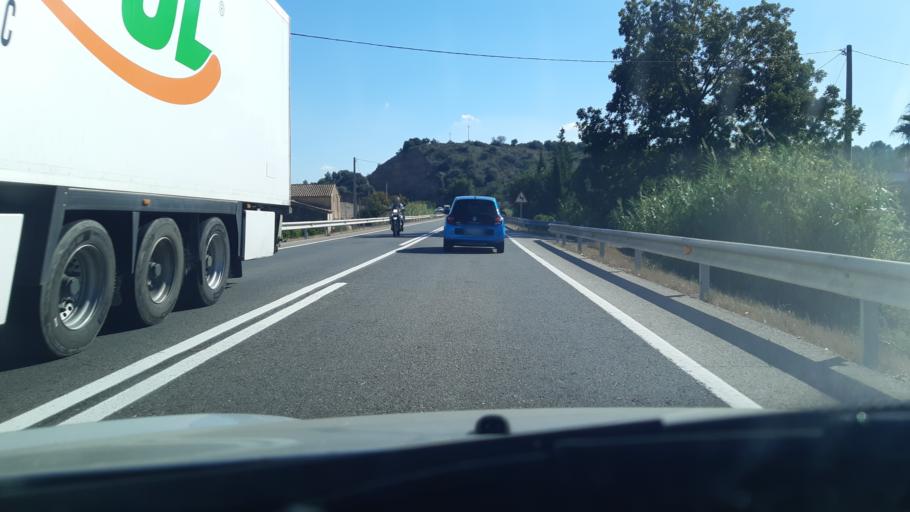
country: ES
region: Catalonia
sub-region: Provincia de Tarragona
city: Tivenys
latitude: 40.8842
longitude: 0.4934
